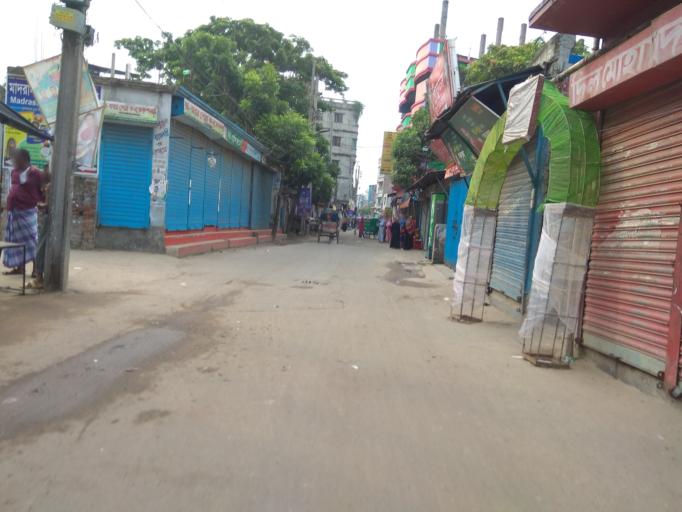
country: BD
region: Dhaka
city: Azimpur
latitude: 23.7151
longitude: 90.3770
